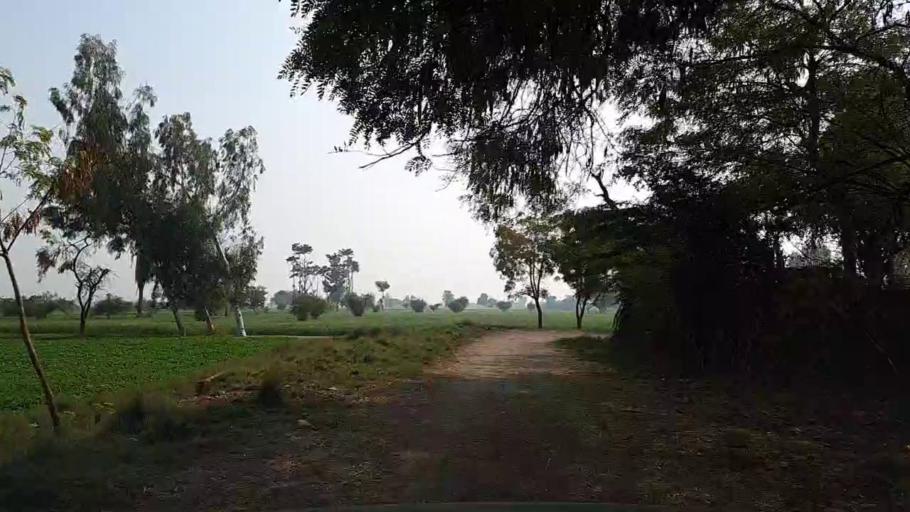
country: PK
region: Sindh
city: Nawabshah
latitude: 26.2761
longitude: 68.4393
